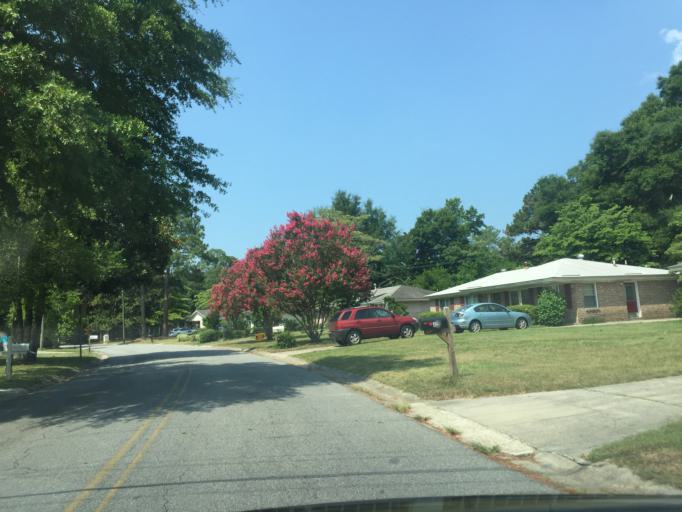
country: US
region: Georgia
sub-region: Chatham County
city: Montgomery
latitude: 31.9878
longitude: -81.1249
